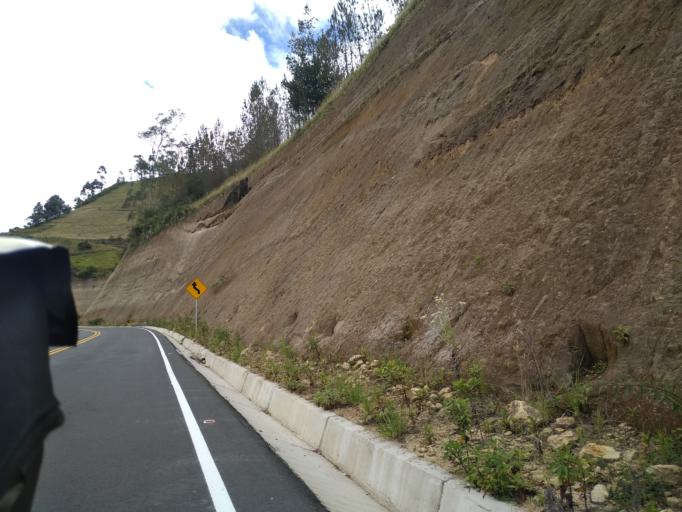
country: EC
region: Cotopaxi
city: Saquisili
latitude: -0.7222
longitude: -78.8929
